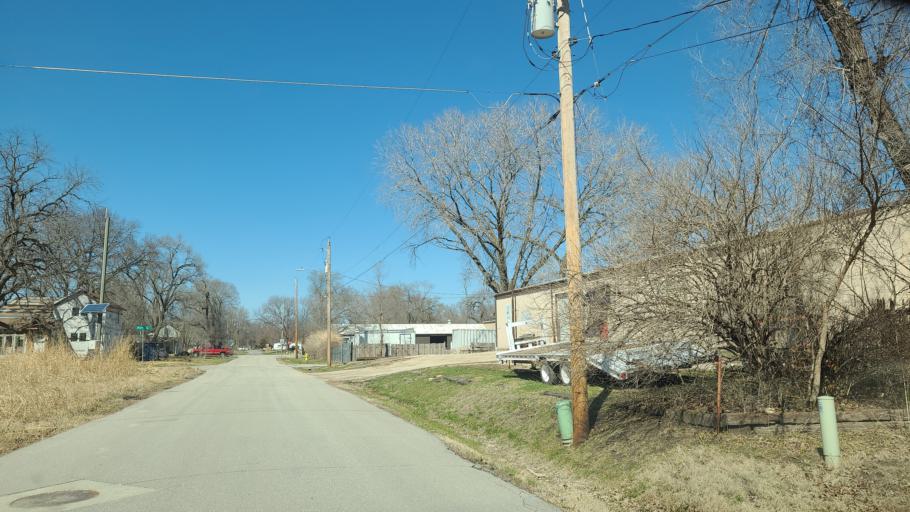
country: US
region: Kansas
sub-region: Douglas County
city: Lawrence
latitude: 38.9792
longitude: -95.2261
